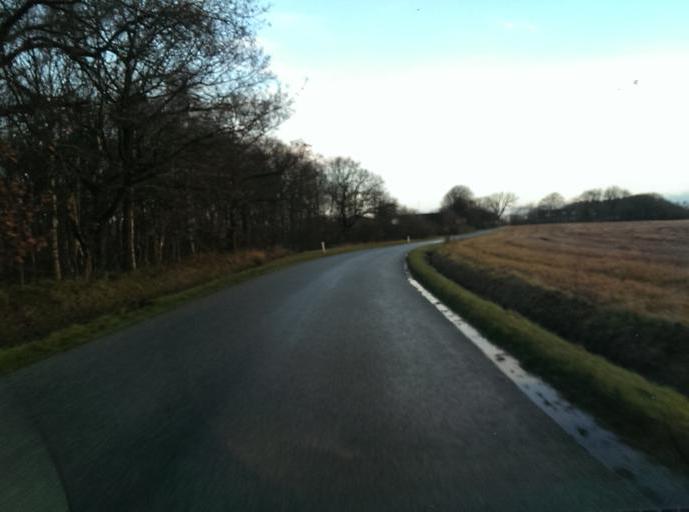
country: DK
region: South Denmark
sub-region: Esbjerg Kommune
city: Tjaereborg
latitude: 55.4789
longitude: 8.6321
